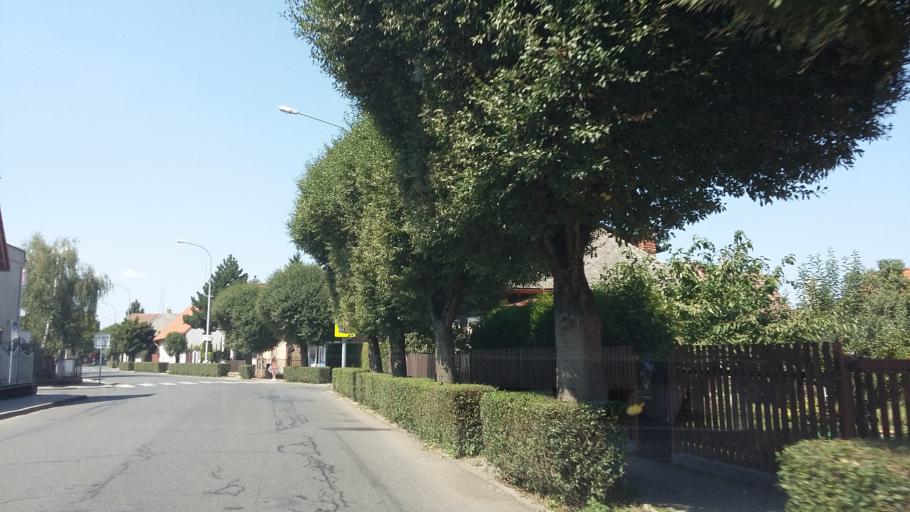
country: CZ
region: Central Bohemia
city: Zelenec
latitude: 50.1314
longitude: 14.6634
